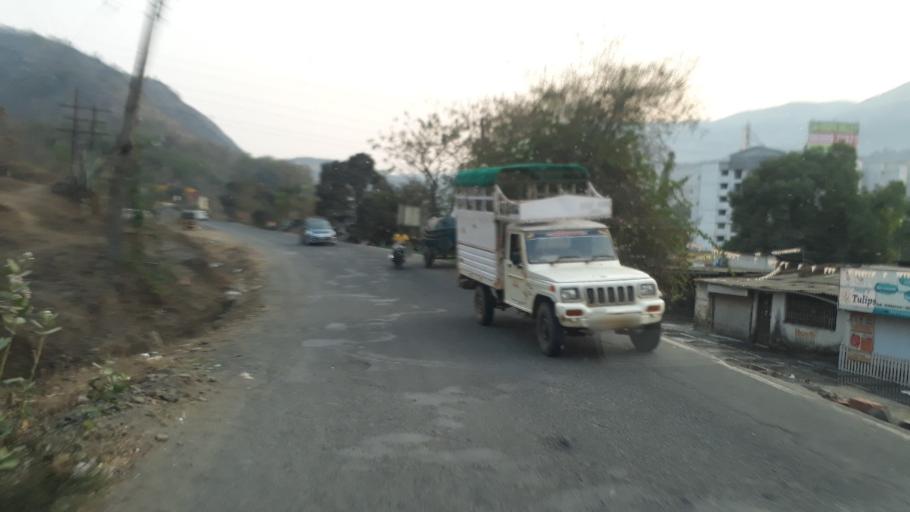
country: IN
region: Maharashtra
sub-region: Raigarh
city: Neral
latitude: 19.0207
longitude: 73.3119
